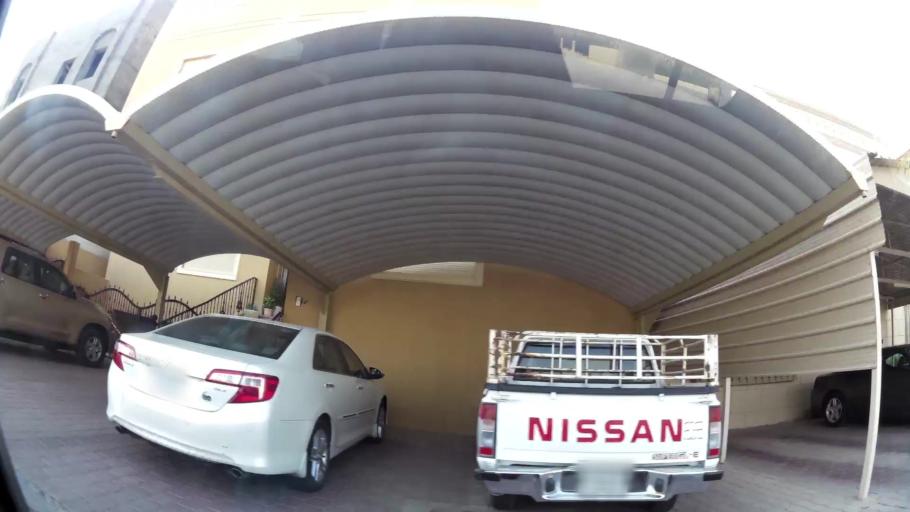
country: KW
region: Muhafazat al Jahra'
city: Al Jahra'
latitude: 29.3221
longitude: 47.7370
